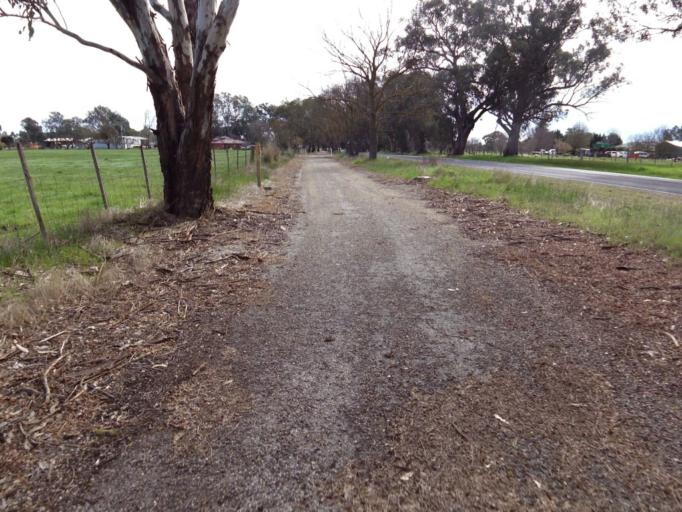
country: AU
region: Victoria
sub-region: Wangaratta
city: Wangaratta
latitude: -36.4324
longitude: 146.3579
